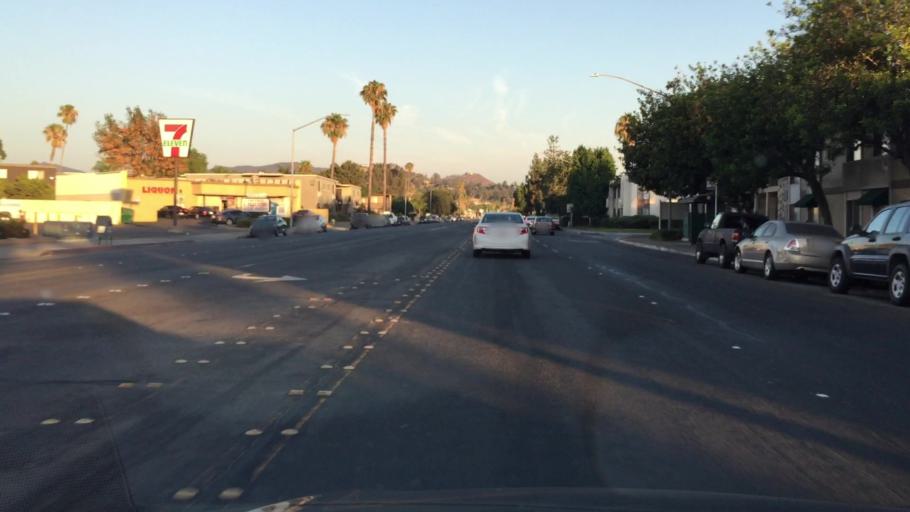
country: US
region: California
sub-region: San Diego County
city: Bostonia
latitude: 32.7923
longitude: -116.9334
